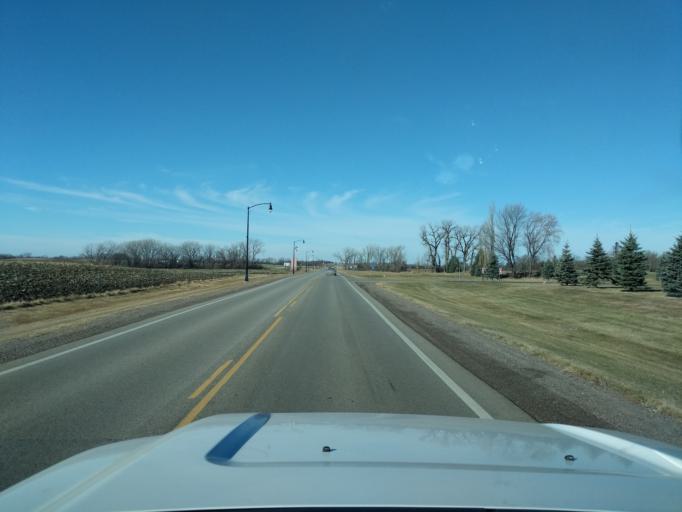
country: US
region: Minnesota
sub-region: Yellow Medicine County
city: Granite Falls
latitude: 44.7653
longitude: -95.5324
